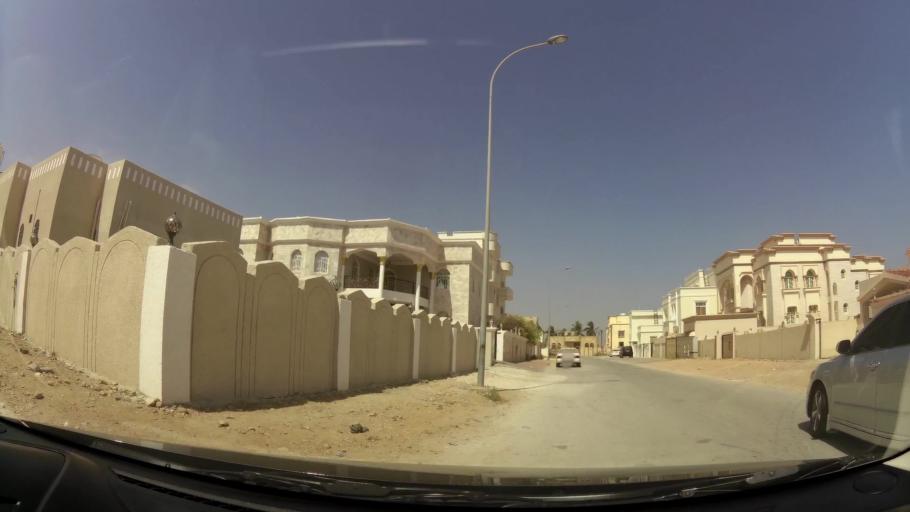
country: OM
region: Zufar
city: Salalah
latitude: 17.0424
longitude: 54.1590
